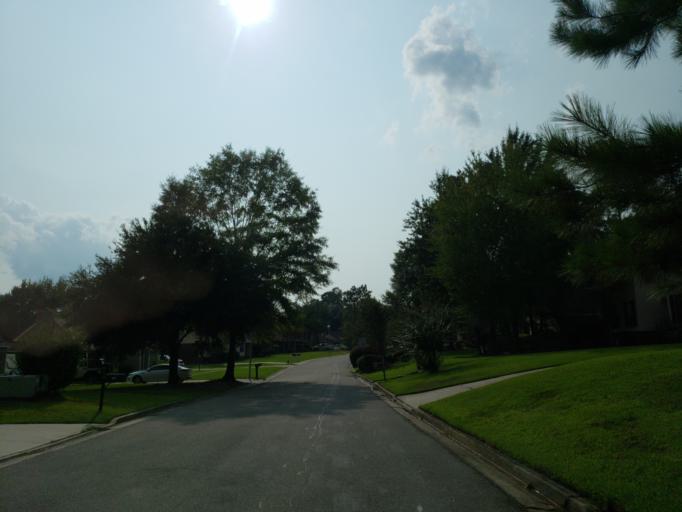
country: US
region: Mississippi
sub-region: Lamar County
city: West Hattiesburg
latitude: 31.3171
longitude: -89.3486
